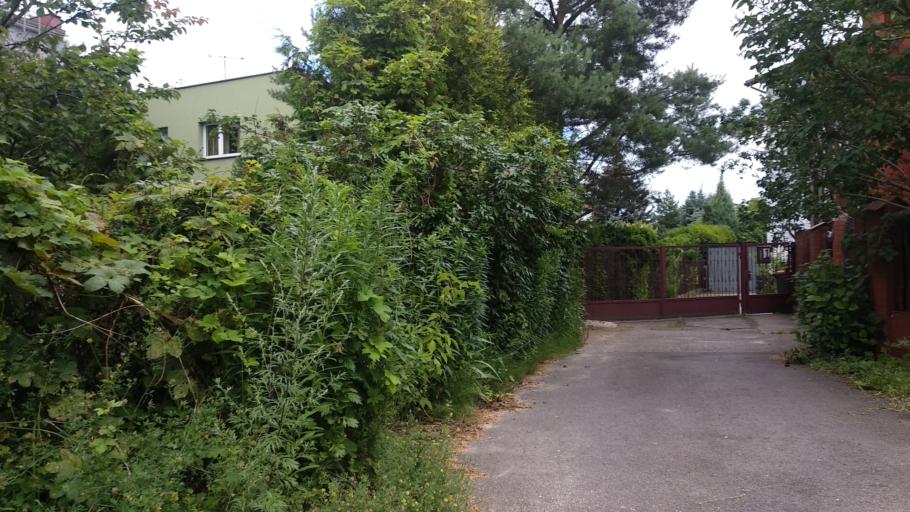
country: PL
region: Lodz Voivodeship
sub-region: Skierniewice
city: Skierniewice
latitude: 51.9431
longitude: 20.1385
